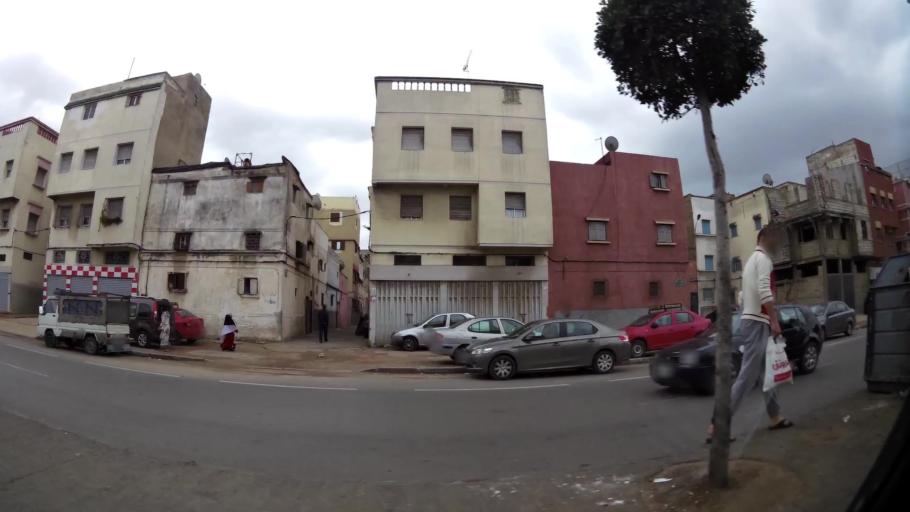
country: MA
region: Grand Casablanca
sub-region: Casablanca
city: Casablanca
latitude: 33.5599
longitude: -7.5533
